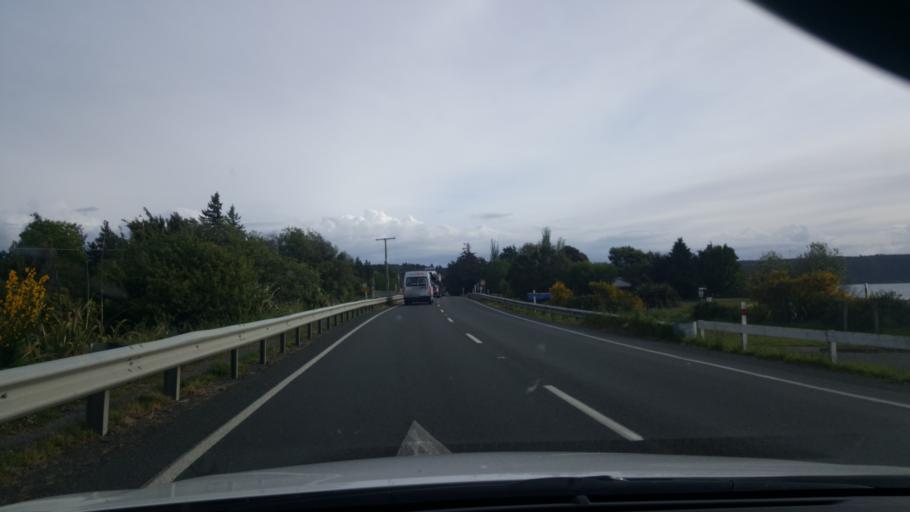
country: NZ
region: Waikato
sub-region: Taupo District
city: Taupo
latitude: -38.7850
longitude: 176.0769
